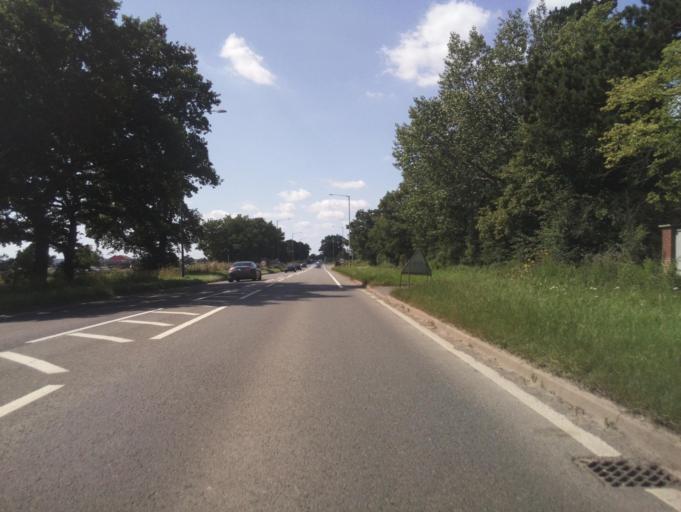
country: GB
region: England
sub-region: Leicestershire
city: Stoke Golding
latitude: 52.5402
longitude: -1.4286
